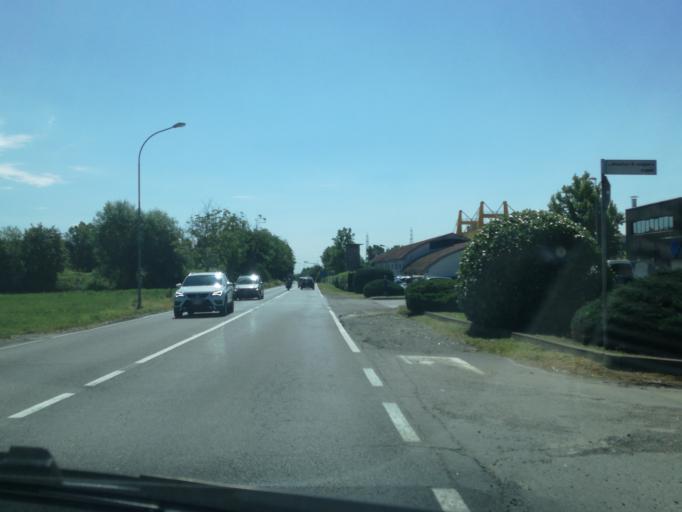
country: IT
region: Lombardy
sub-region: Provincia di Bergamo
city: Piazza Caduti
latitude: 45.6978
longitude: 9.4999
